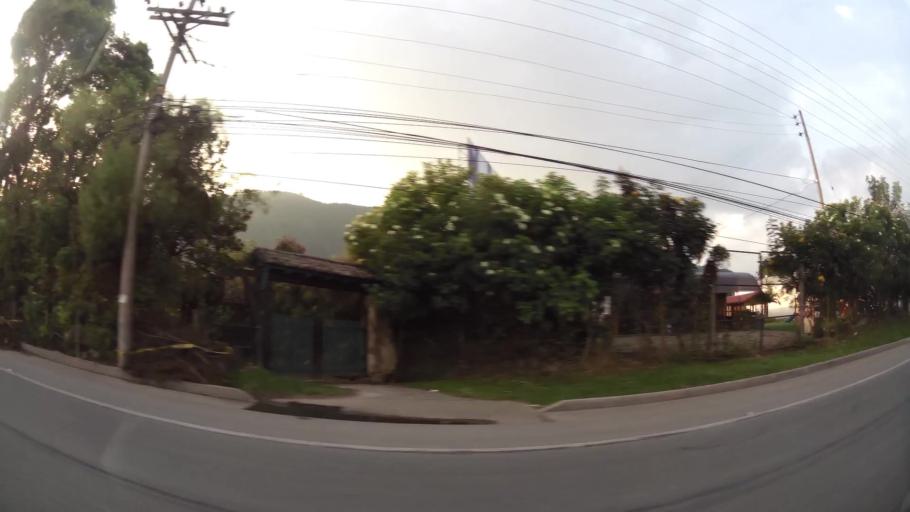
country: CO
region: Cundinamarca
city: Cota
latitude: 4.7962
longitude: -74.1135
